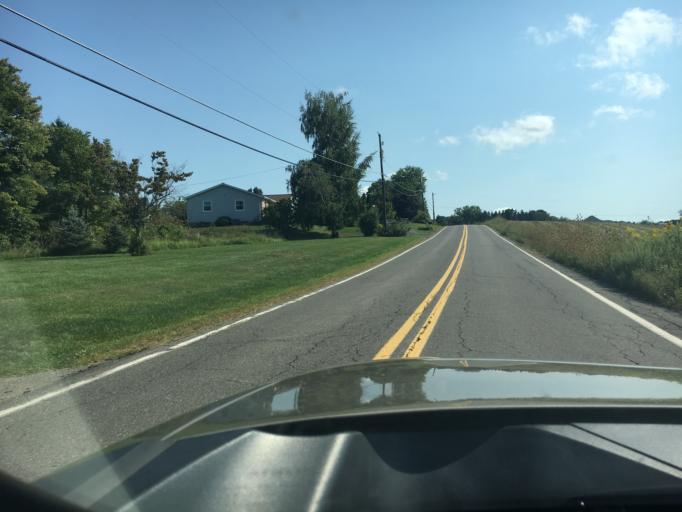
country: US
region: Pennsylvania
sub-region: Luzerne County
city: Conyngham
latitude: 41.0055
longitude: -76.0642
